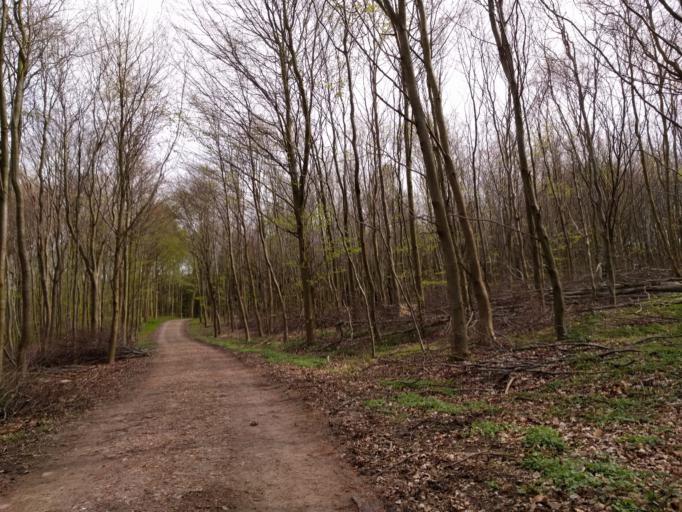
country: DK
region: South Denmark
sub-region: Kerteminde Kommune
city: Munkebo
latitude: 55.4319
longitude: 10.5587
